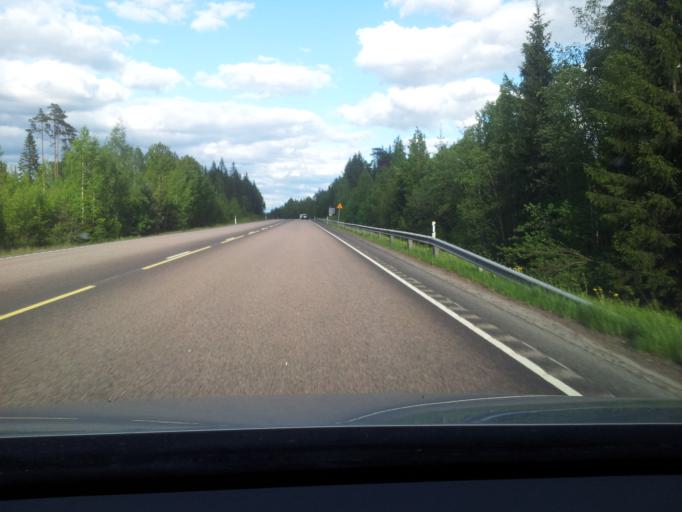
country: FI
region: South Karelia
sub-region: Lappeenranta
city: Taavetti
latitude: 60.9134
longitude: 27.3719
